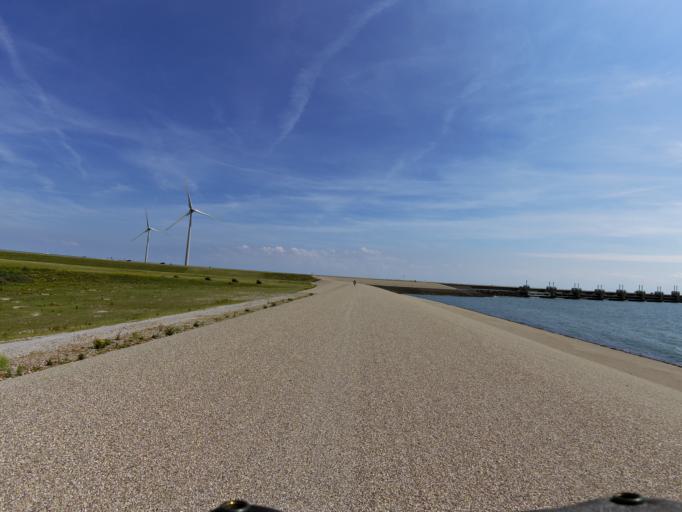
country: NL
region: Zeeland
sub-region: Schouwen-Duiveland
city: Burgh
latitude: 51.6528
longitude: 3.7167
